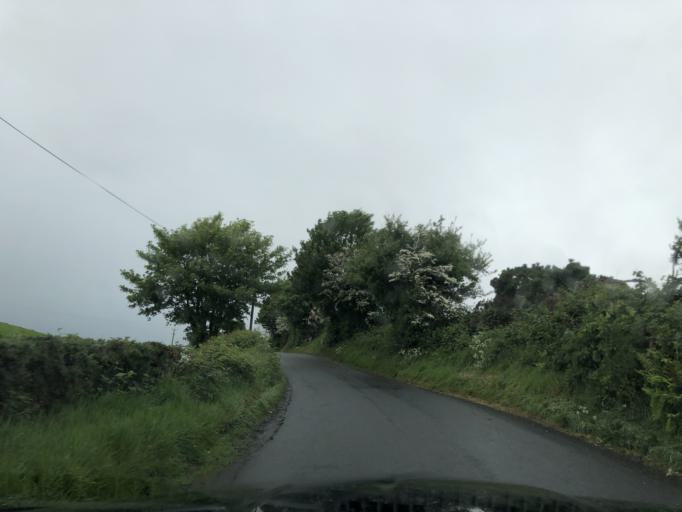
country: GB
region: Northern Ireland
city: Dunloy
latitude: 55.1350
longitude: -6.3685
